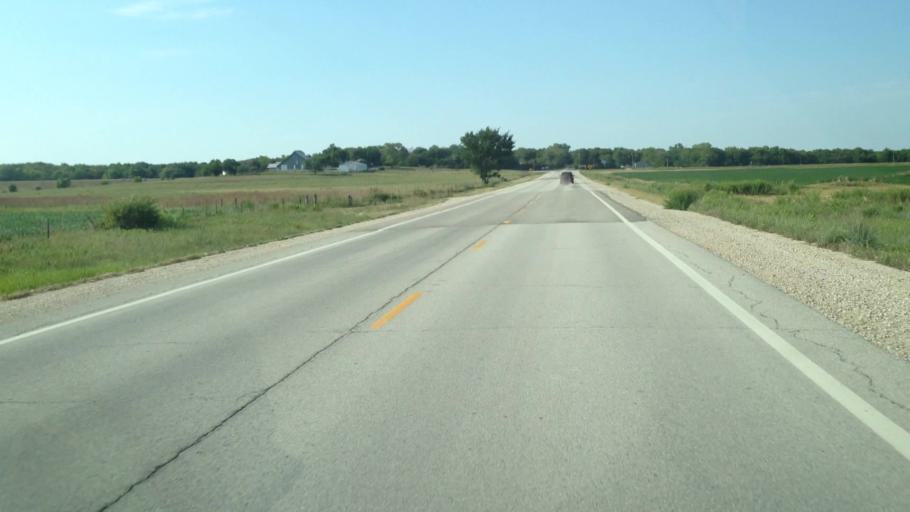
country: US
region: Kansas
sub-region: Anderson County
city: Garnett
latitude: 38.0758
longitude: -95.1694
